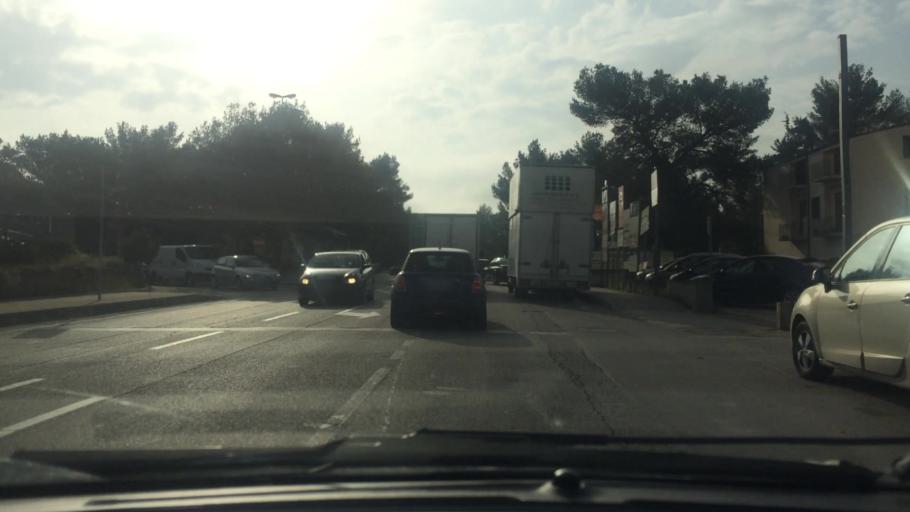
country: IT
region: Basilicate
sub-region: Provincia di Matera
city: Matera
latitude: 40.6805
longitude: 16.5844
